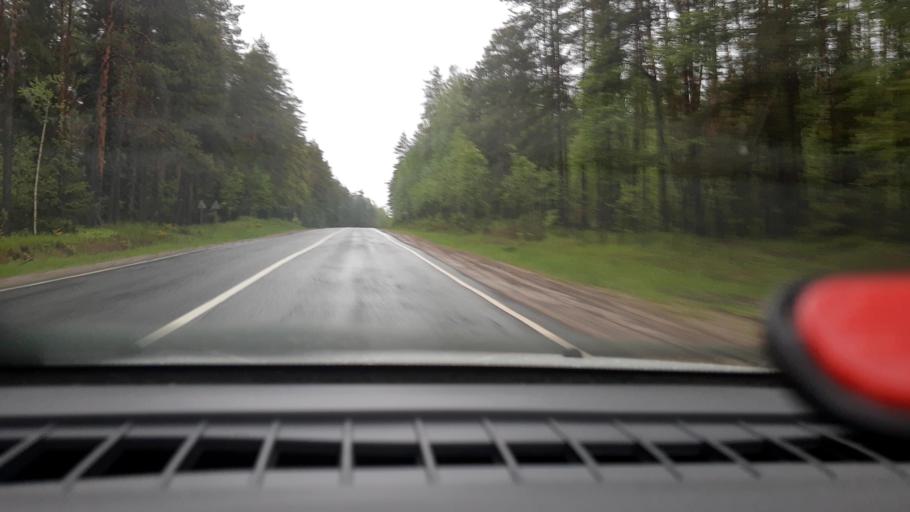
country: RU
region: Nizjnij Novgorod
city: Krasnyye Baki
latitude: 56.9897
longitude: 45.1166
